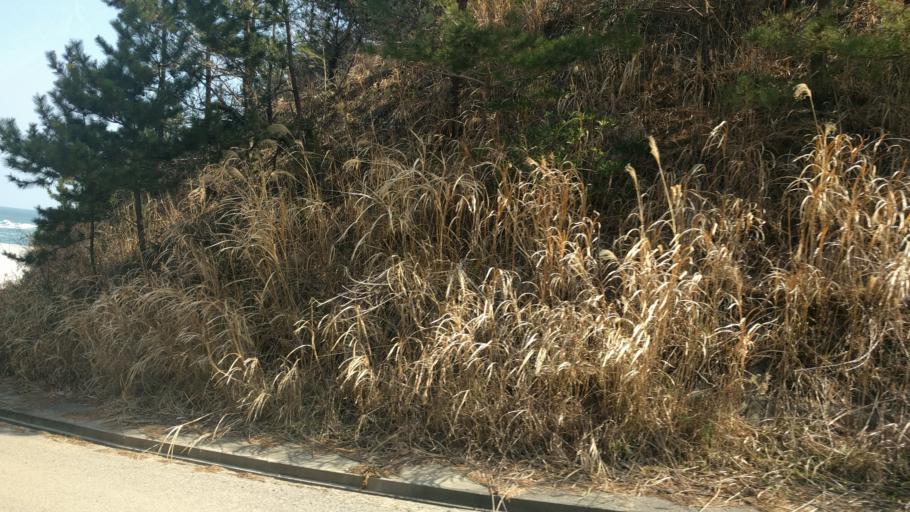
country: JP
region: Fukushima
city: Iwaki
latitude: 37.1543
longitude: 141.0002
